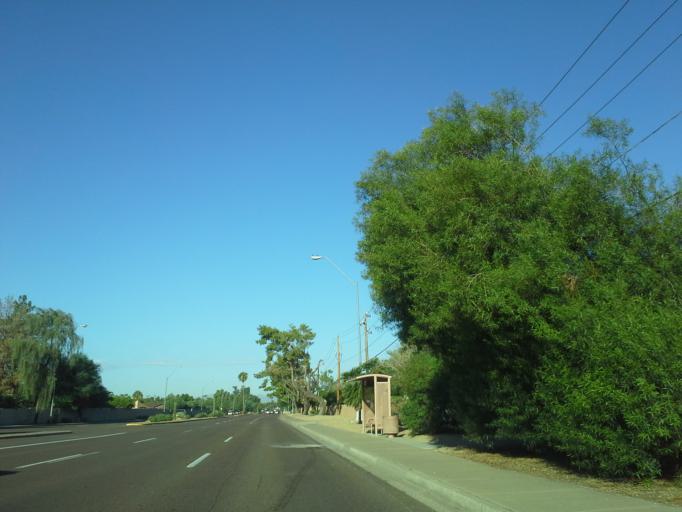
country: US
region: Arizona
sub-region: Maricopa County
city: Glendale
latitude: 33.6080
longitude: -112.0691
